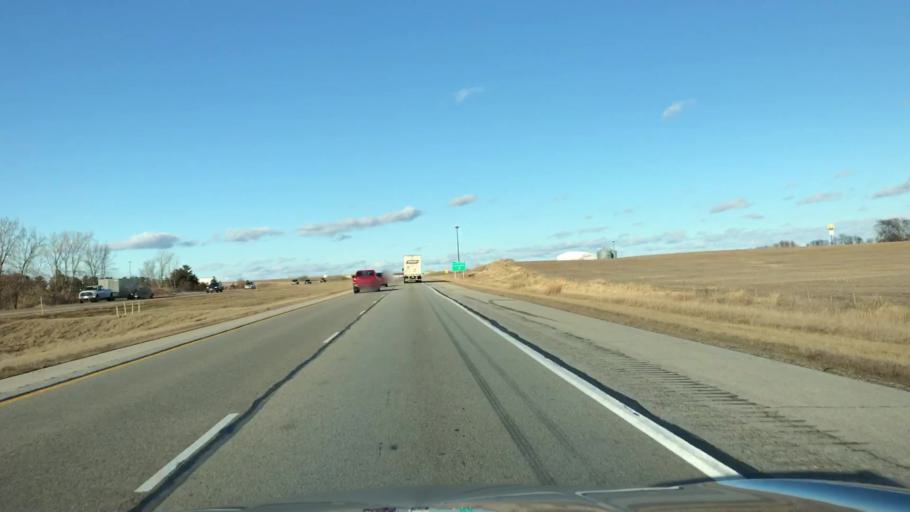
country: US
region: Illinois
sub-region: McLean County
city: Lexington
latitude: 40.6385
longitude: -88.8124
